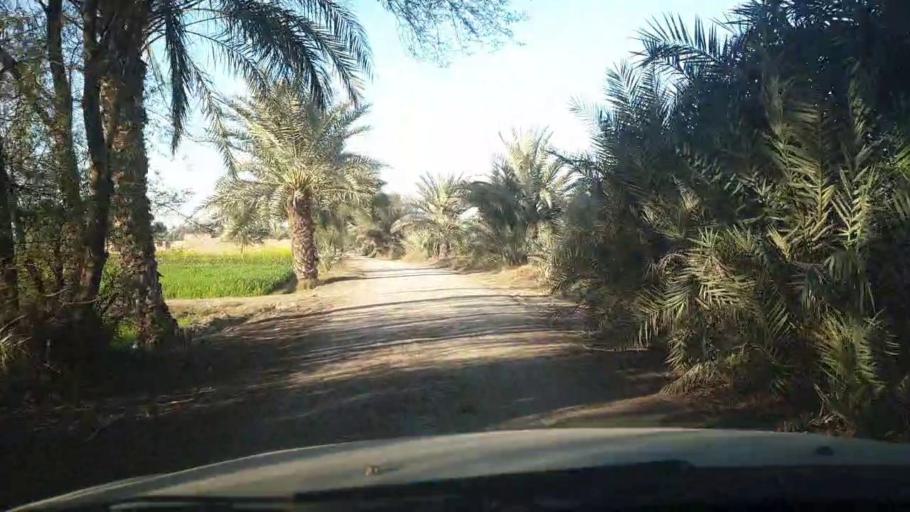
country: PK
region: Sindh
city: Ghotki
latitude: 28.0246
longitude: 69.3082
